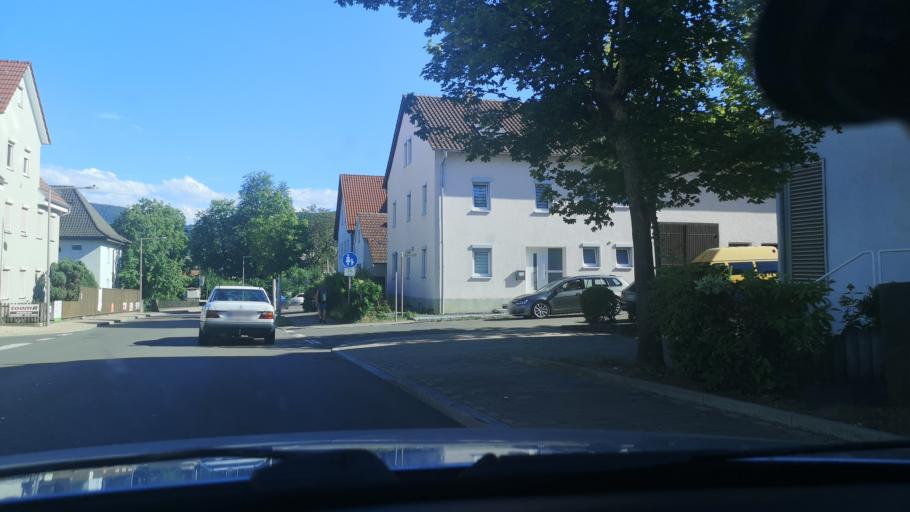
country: DE
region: Baden-Wuerttemberg
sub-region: Regierungsbezirk Stuttgart
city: Heiningen
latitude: 48.6599
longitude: 9.6516
